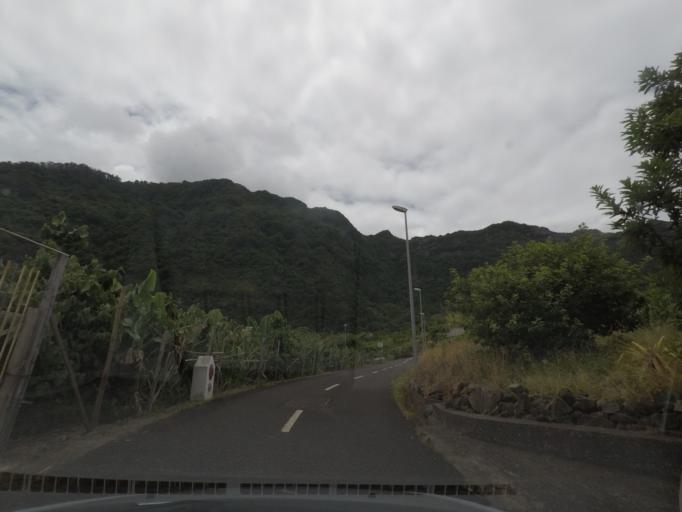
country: PT
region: Madeira
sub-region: Santana
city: Santana
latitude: 32.8285
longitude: -16.9527
